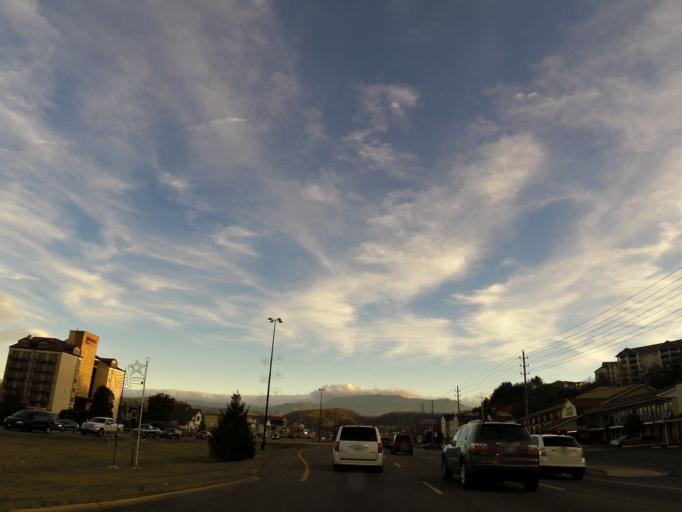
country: US
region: Tennessee
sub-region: Sevier County
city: Pigeon Forge
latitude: 35.7878
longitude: -83.5556
